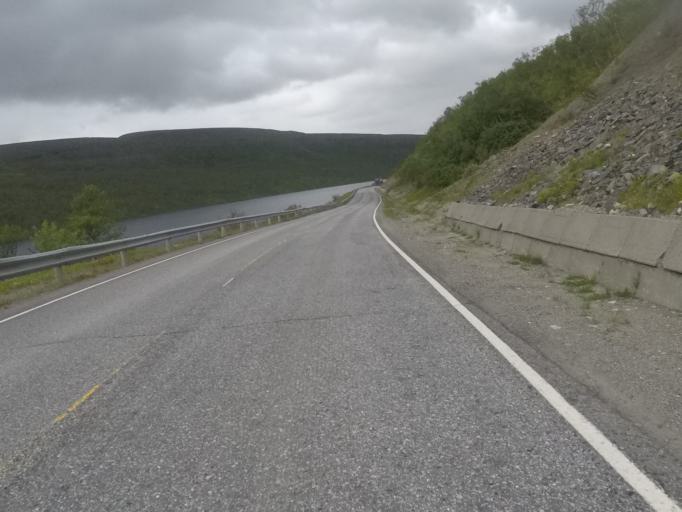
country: NO
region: Finnmark Fylke
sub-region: Alta
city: Alta
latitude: 69.7016
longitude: 23.4100
